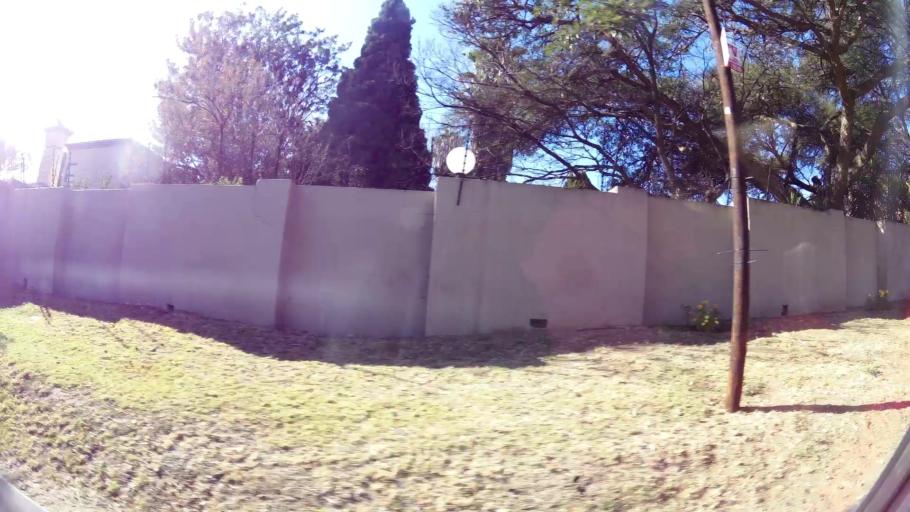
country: ZA
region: Gauteng
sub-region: City of Johannesburg Metropolitan Municipality
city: Diepsloot
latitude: -26.0397
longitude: 27.9700
